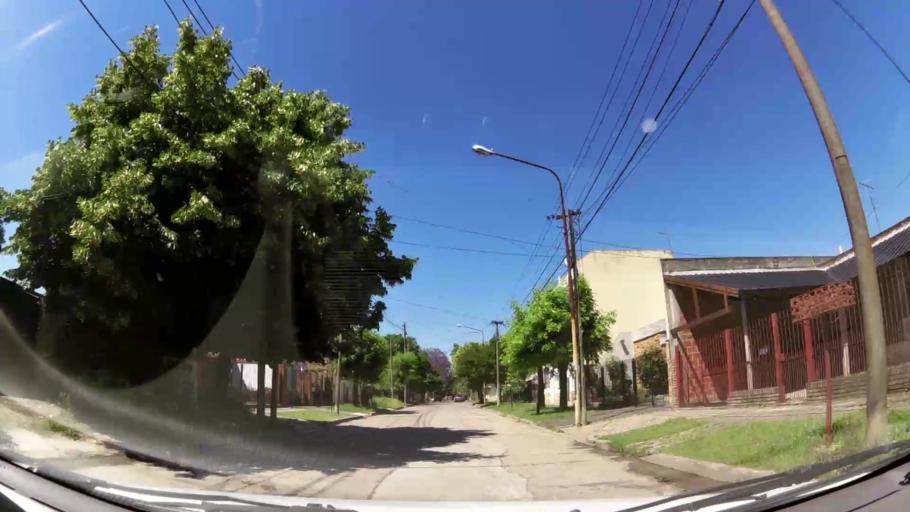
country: AR
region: Buenos Aires
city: Ituzaingo
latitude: -34.6778
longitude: -58.6590
